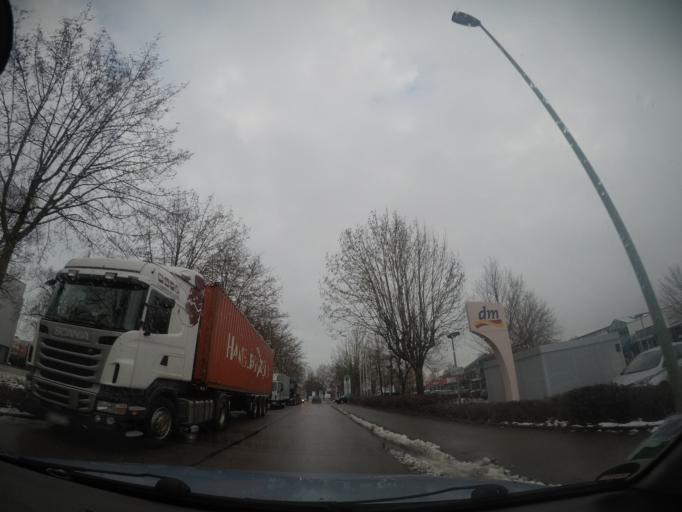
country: DE
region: Bavaria
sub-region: Swabia
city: Neu-Ulm
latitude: 48.3759
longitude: 10.0070
